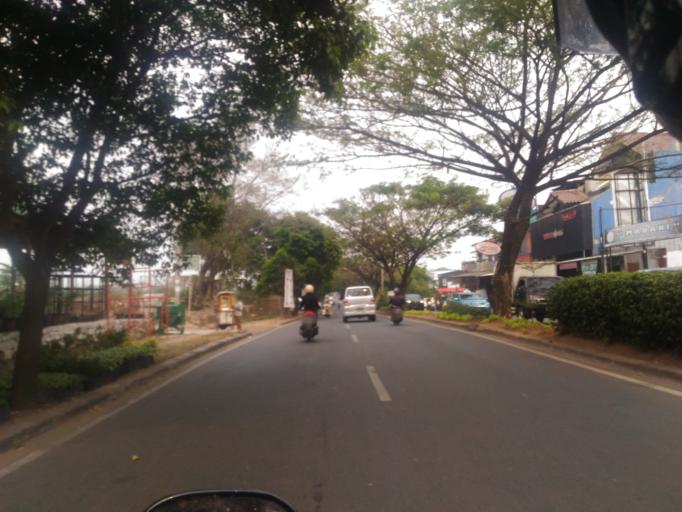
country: ID
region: West Java
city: Depok
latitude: -6.3805
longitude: 106.8554
